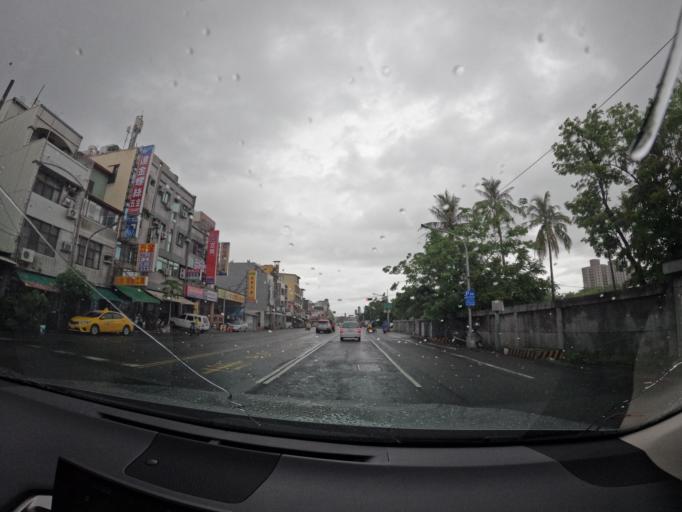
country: TW
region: Taiwan
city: Fengshan
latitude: 22.6437
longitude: 120.3646
